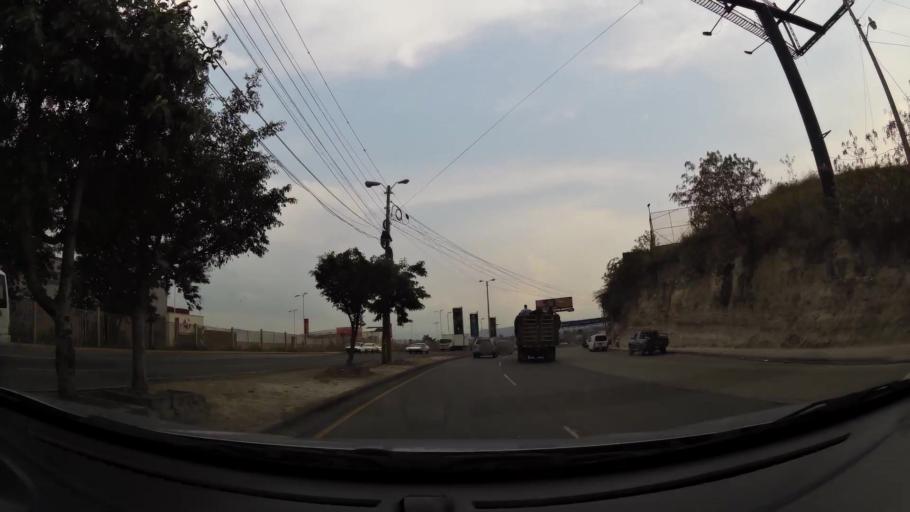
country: HN
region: Francisco Morazan
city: Tegucigalpa
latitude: 14.0754
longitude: -87.2139
